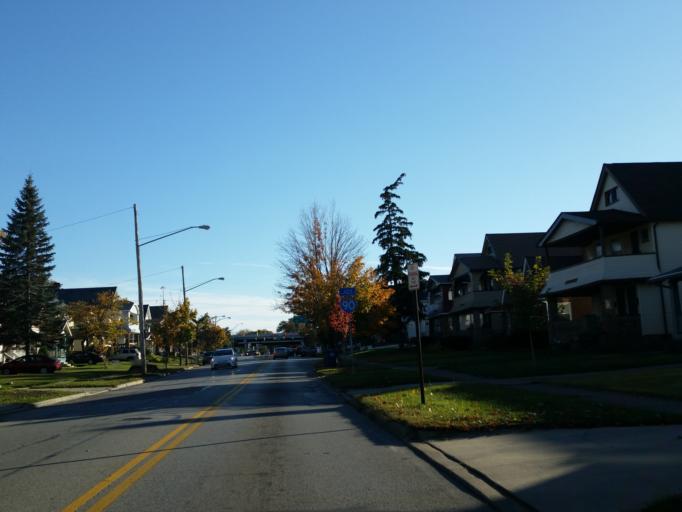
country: US
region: Ohio
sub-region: Cuyahoga County
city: Lakewood
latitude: 41.4722
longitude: -81.7898
